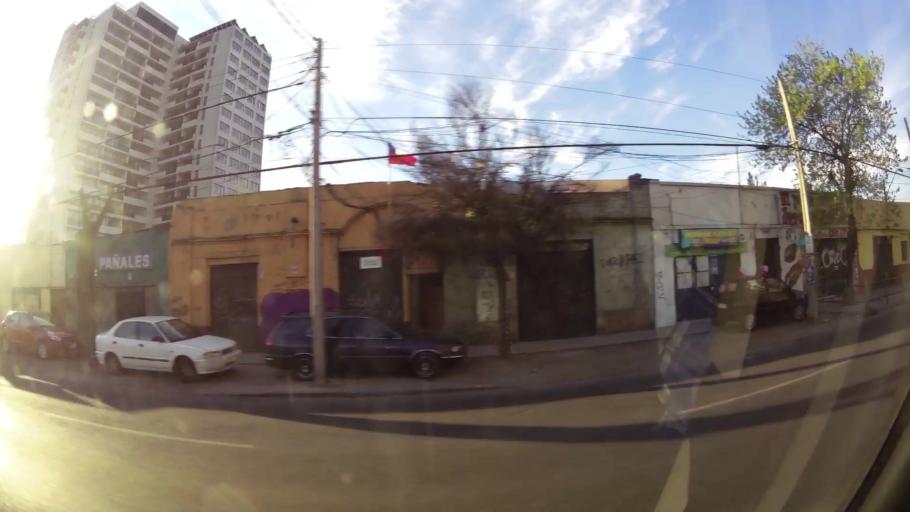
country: CL
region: Santiago Metropolitan
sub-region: Provincia de Santiago
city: Lo Prado
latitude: -33.4374
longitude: -70.6887
